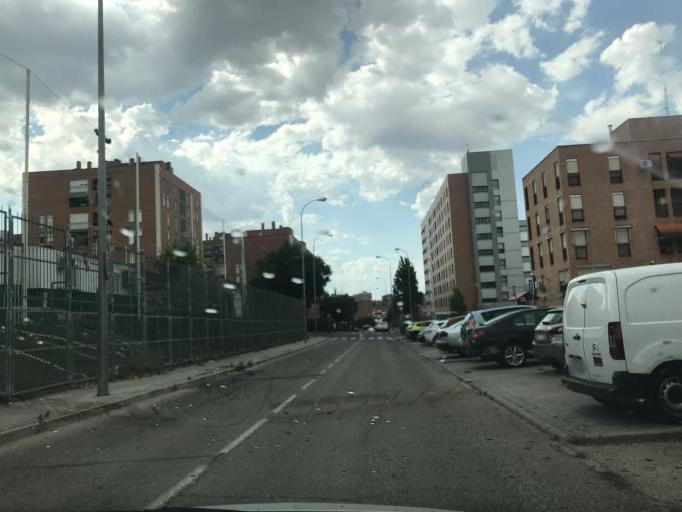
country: ES
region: Madrid
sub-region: Provincia de Madrid
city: Pinar de Chamartin
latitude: 40.4726
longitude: -3.6581
